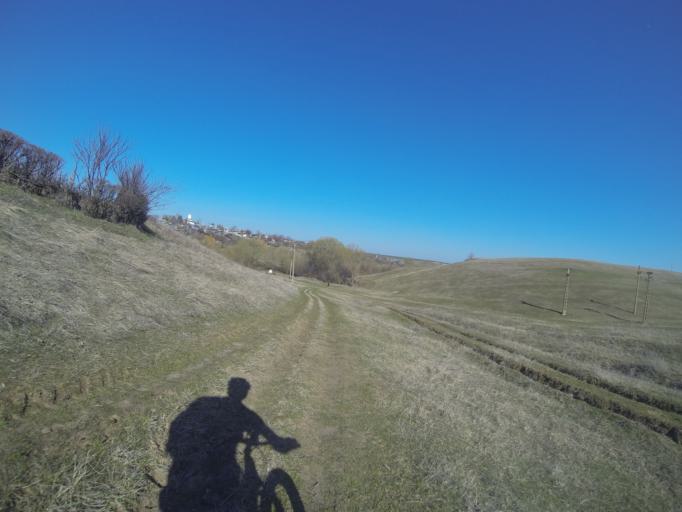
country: RO
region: Dolj
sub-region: Comuna Segarcea
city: Segarcea
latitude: 44.1253
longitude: 23.7905
